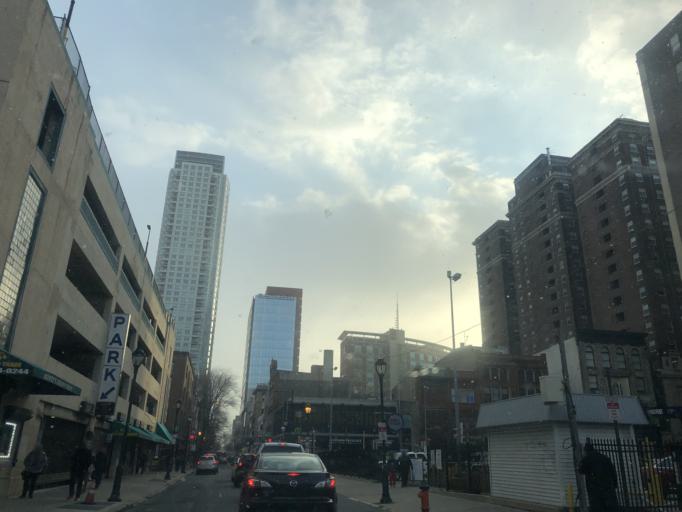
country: US
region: Pennsylvania
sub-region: Philadelphia County
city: Philadelphia
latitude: 39.9503
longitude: -75.1537
